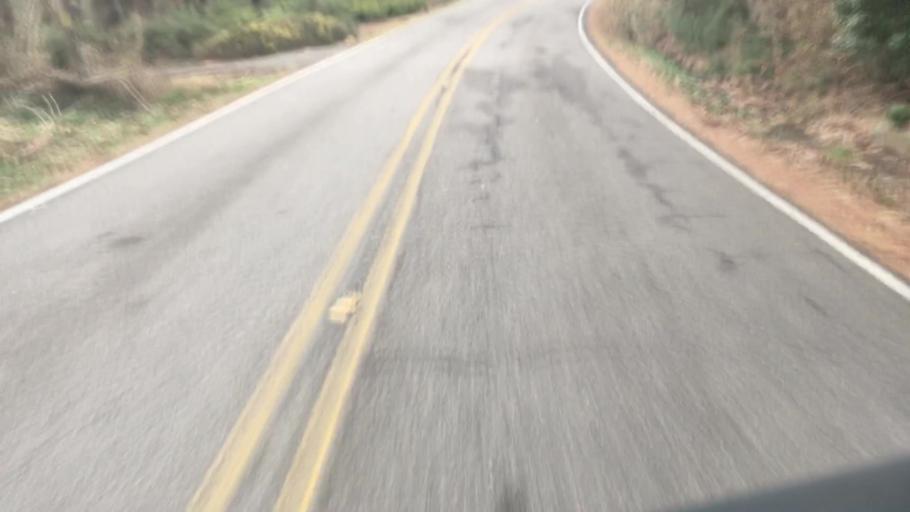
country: US
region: Alabama
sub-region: Jefferson County
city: Vestavia Hills
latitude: 33.4149
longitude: -86.7643
